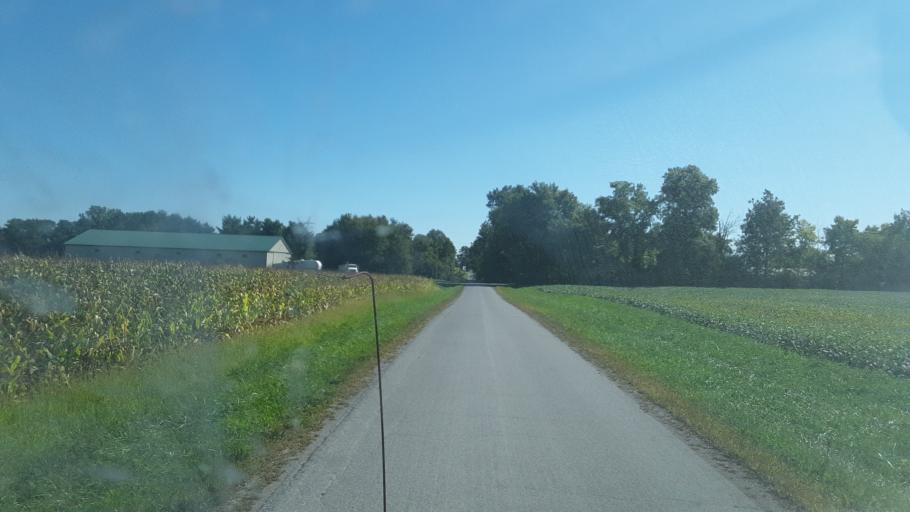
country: US
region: Ohio
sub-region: Wyandot County
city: Upper Sandusky
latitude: 40.9350
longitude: -83.2005
